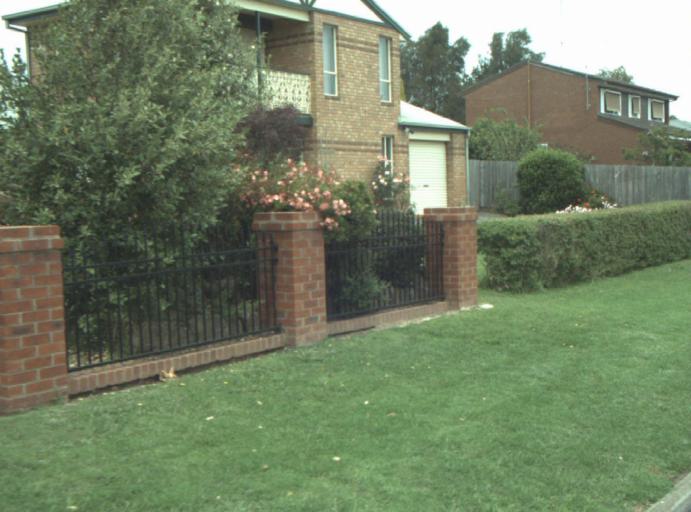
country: AU
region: Victoria
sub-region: Greater Geelong
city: Clifton Springs
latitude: -38.1501
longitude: 144.5741
